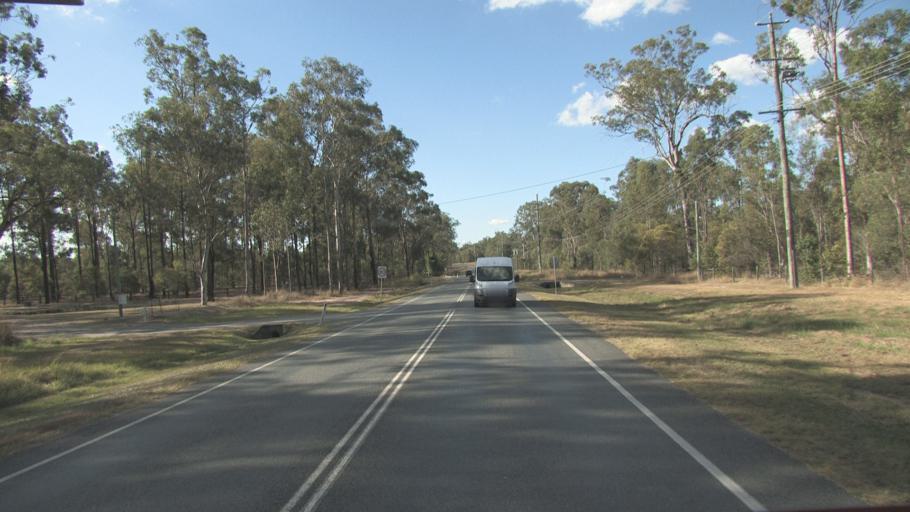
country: AU
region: Queensland
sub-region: Logan
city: North Maclean
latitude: -27.8109
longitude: 152.9786
